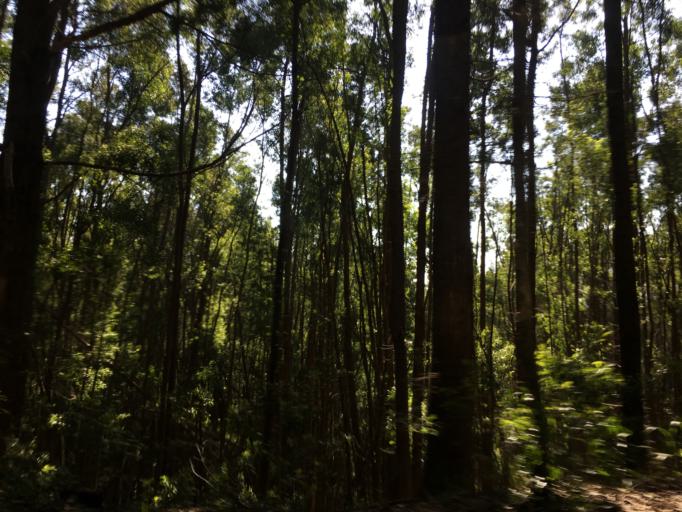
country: PT
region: Lisbon
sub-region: Sintra
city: Colares
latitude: 38.7773
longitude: -9.4376
